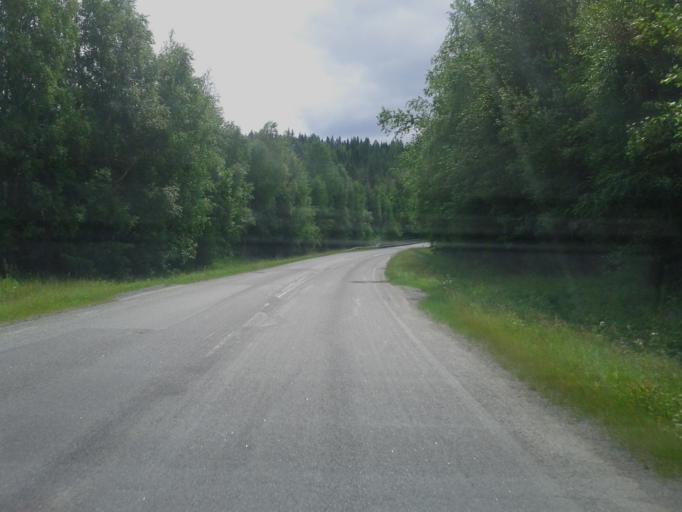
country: SE
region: Vaesternorrland
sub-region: OErnskoeldsviks Kommun
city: Bjasta
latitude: 63.2436
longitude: 18.4349
